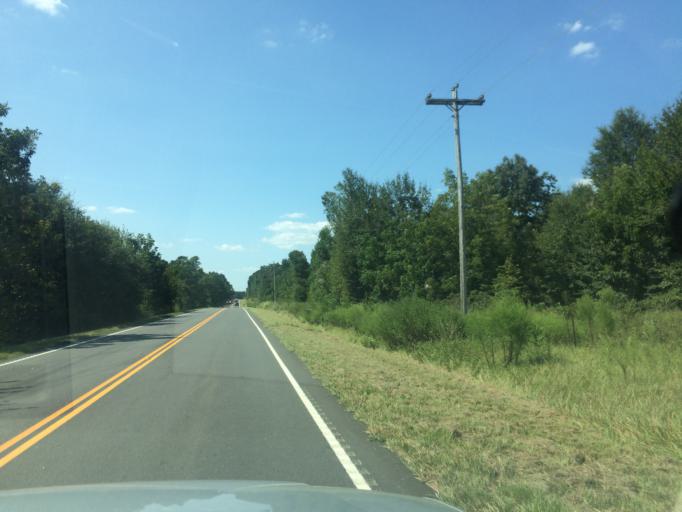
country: US
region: South Carolina
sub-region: Lexington County
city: Batesburg-Leesville
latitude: 33.7048
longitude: -81.4850
